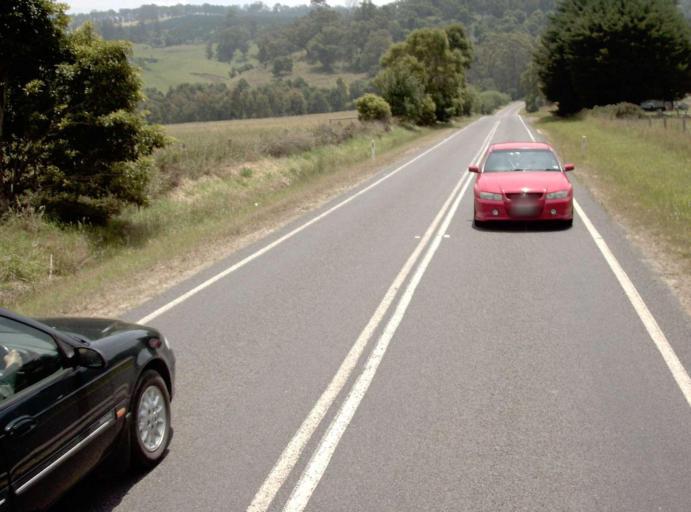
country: AU
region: Victoria
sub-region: Latrobe
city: Traralgon
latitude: -38.3769
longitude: 146.7544
